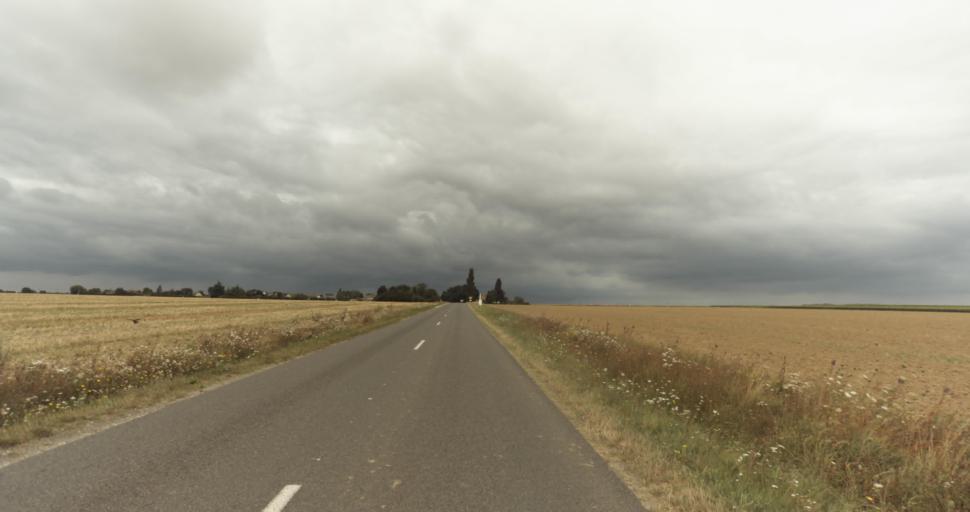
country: FR
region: Haute-Normandie
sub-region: Departement de l'Eure
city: Gravigny
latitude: 49.0482
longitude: 1.2292
